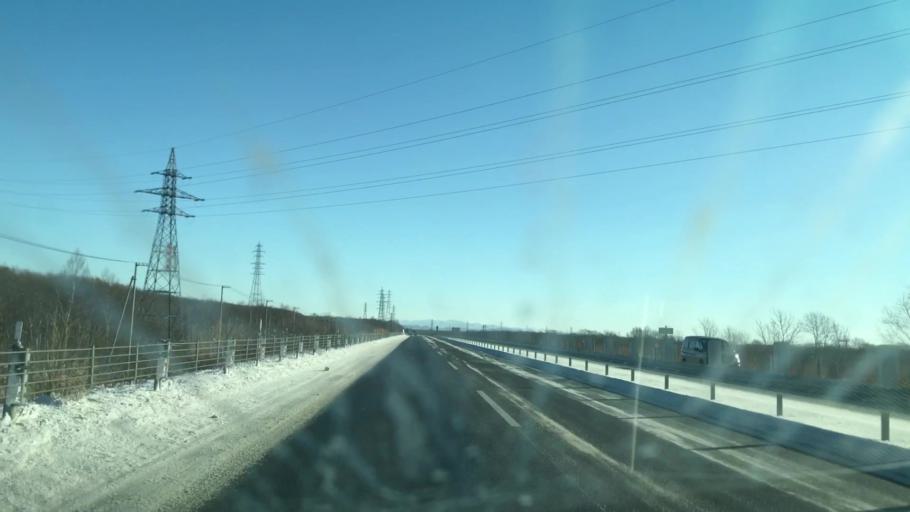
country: JP
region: Hokkaido
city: Tomakomai
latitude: 42.6734
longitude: 141.7623
